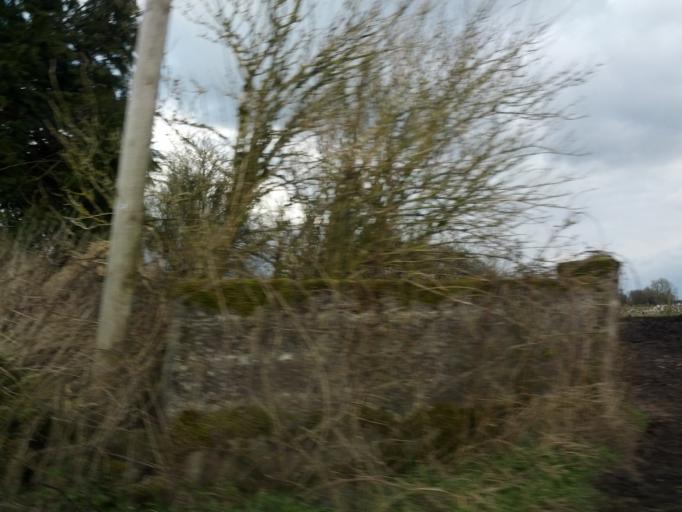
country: IE
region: Connaught
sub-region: County Galway
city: Athenry
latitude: 53.4582
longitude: -8.6434
